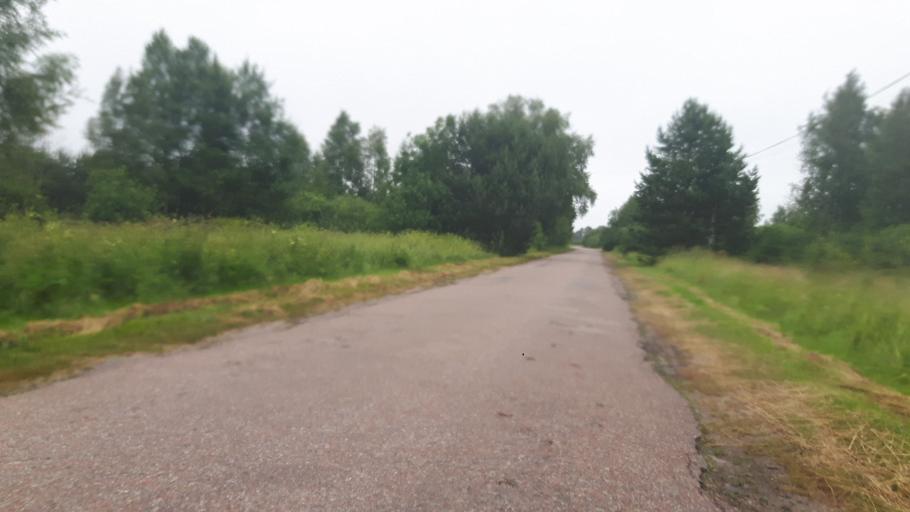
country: LV
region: Nica
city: Nica
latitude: 56.3880
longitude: 20.9985
